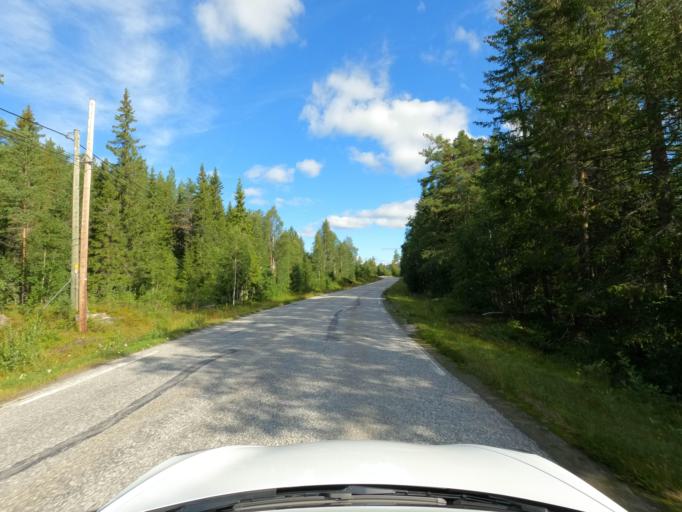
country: NO
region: Telemark
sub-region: Tinn
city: Rjukan
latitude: 59.9641
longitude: 8.8761
